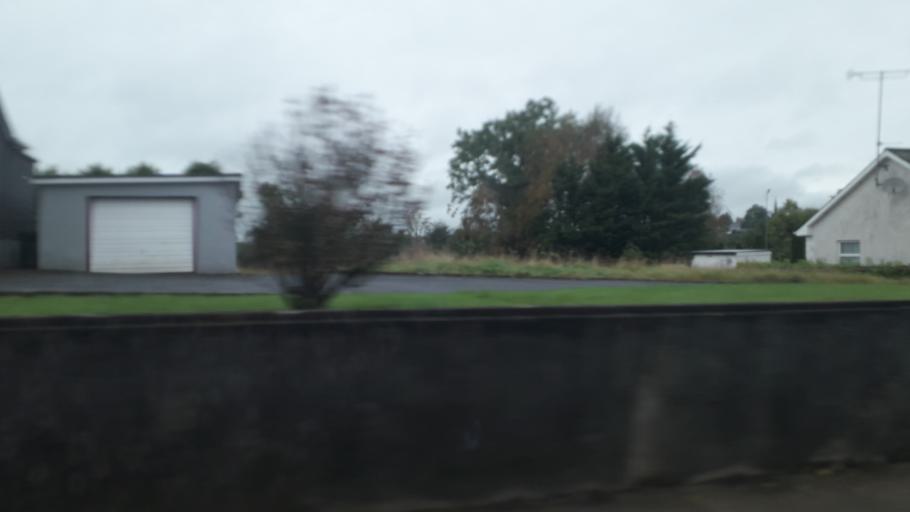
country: IE
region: Leinster
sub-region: An Longfort
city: Lanesborough
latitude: 53.7730
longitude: -8.1033
